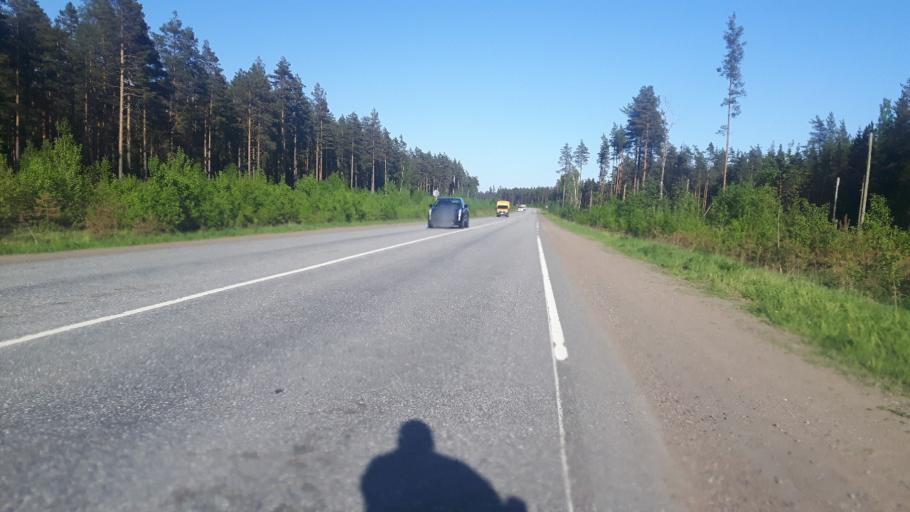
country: RU
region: Leningrad
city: Molodezhnoye
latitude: 60.1727
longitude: 29.2947
